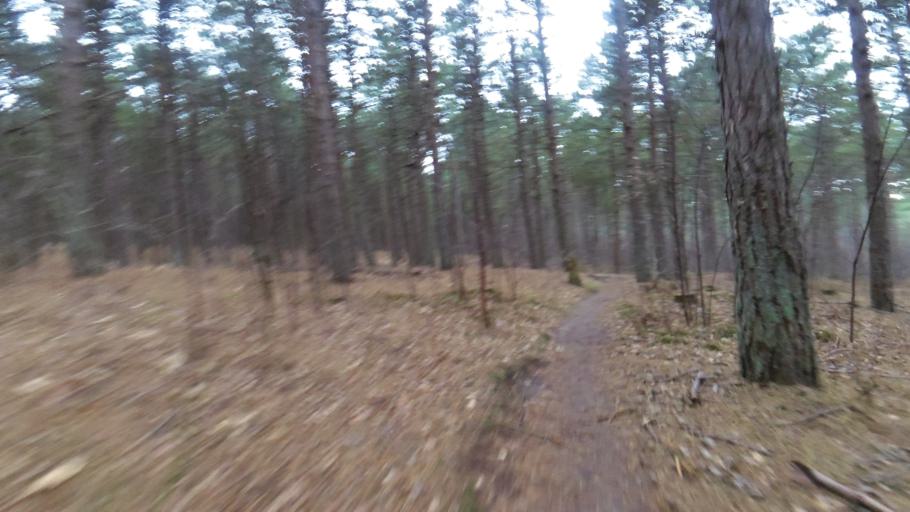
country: NL
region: North Holland
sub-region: Gemeente Bergen
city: Egmond aan Zee
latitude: 52.6864
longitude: 4.6686
